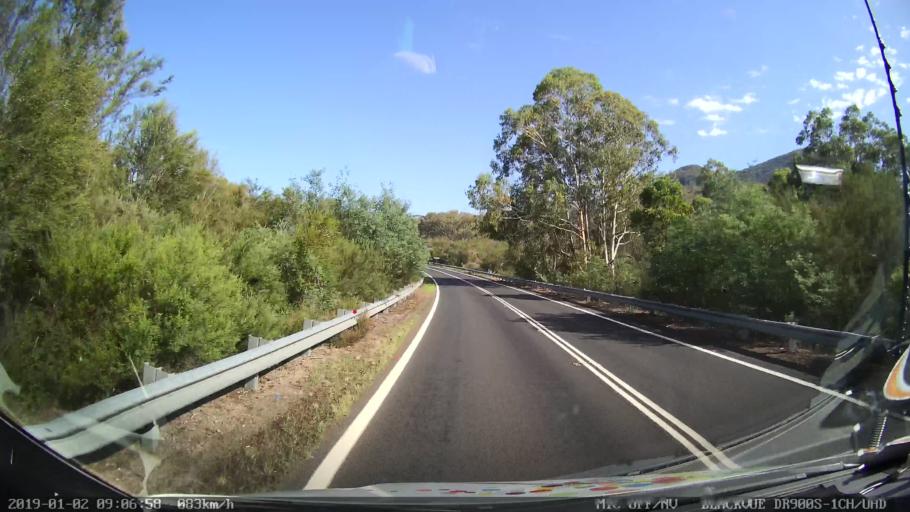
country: AU
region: New South Wales
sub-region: Tumut Shire
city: Tumut
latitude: -35.5448
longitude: 148.3030
